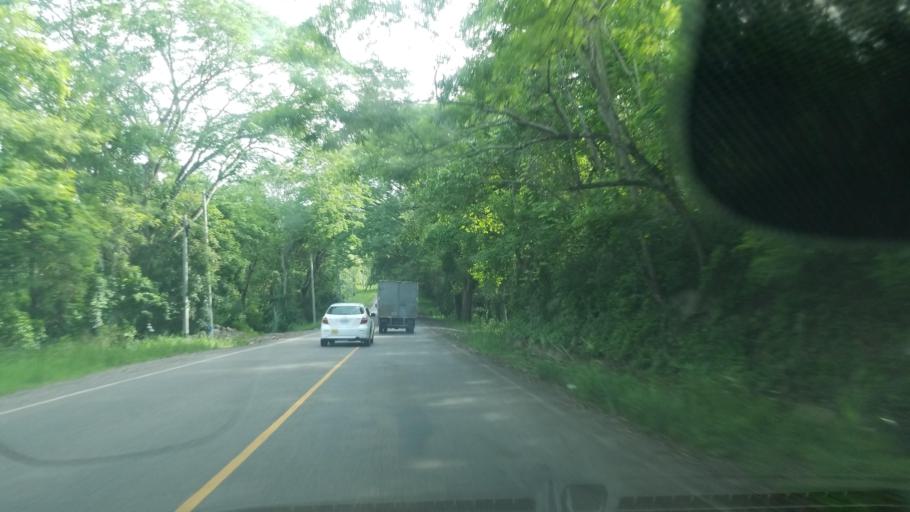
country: HN
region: Santa Barbara
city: Ilama
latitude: 15.0859
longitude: -88.2161
